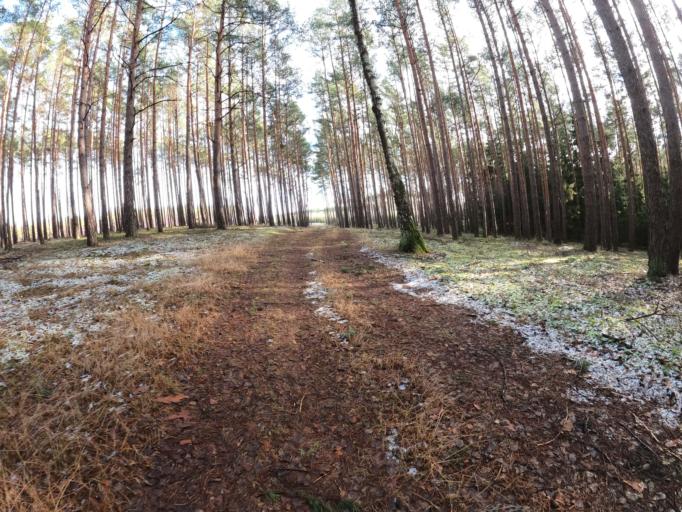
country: PL
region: Lubusz
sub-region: Powiat slubicki
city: Cybinka
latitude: 52.2449
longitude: 14.8073
